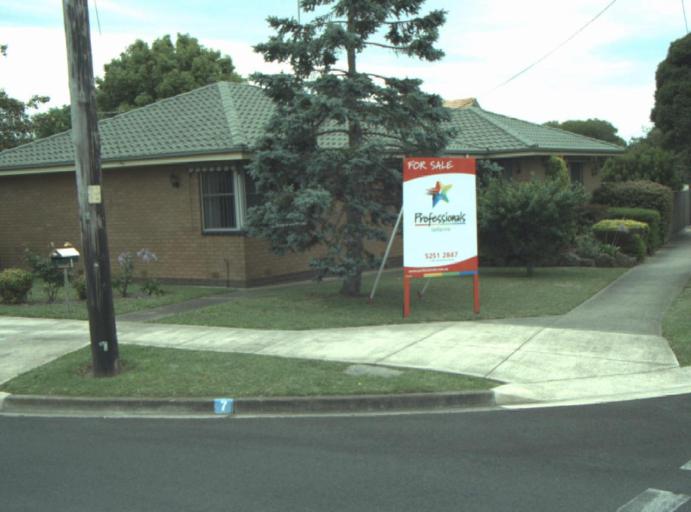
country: AU
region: Victoria
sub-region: Greater Geelong
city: Leopold
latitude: -38.1867
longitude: 144.4702
